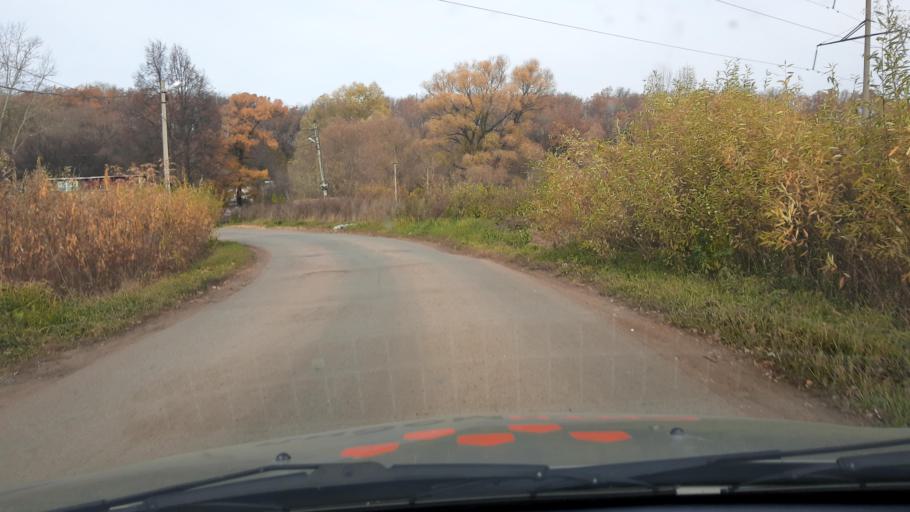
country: RU
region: Bashkortostan
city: Avdon
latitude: 54.7047
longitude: 55.7946
